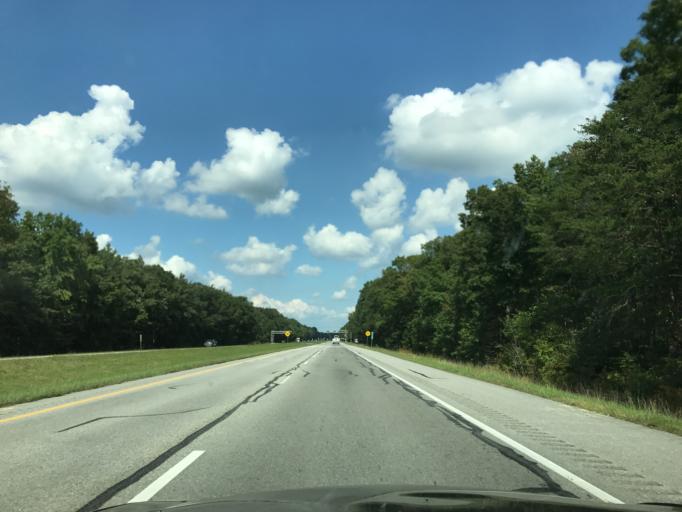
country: US
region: Delaware
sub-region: New Castle County
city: Townsend
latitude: 39.3085
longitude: -75.8494
